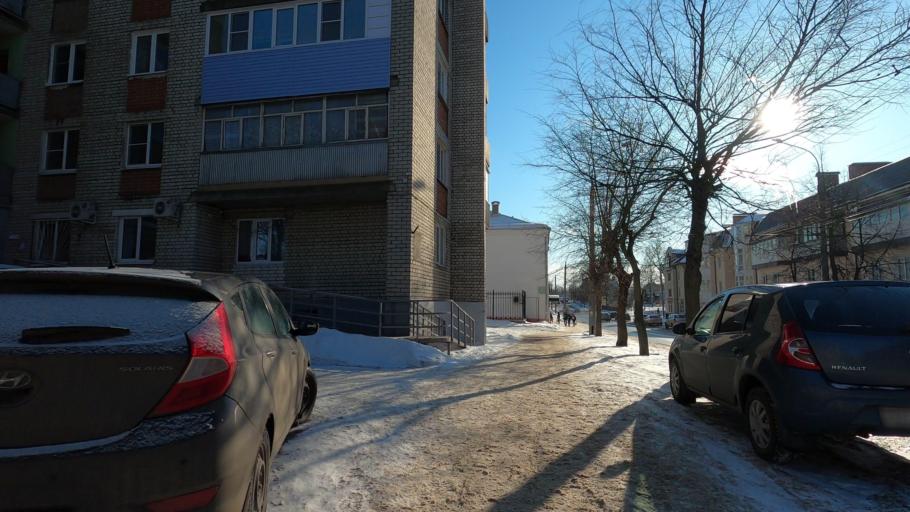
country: RU
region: Jaroslavl
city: Rybinsk
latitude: 58.0460
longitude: 38.8386
